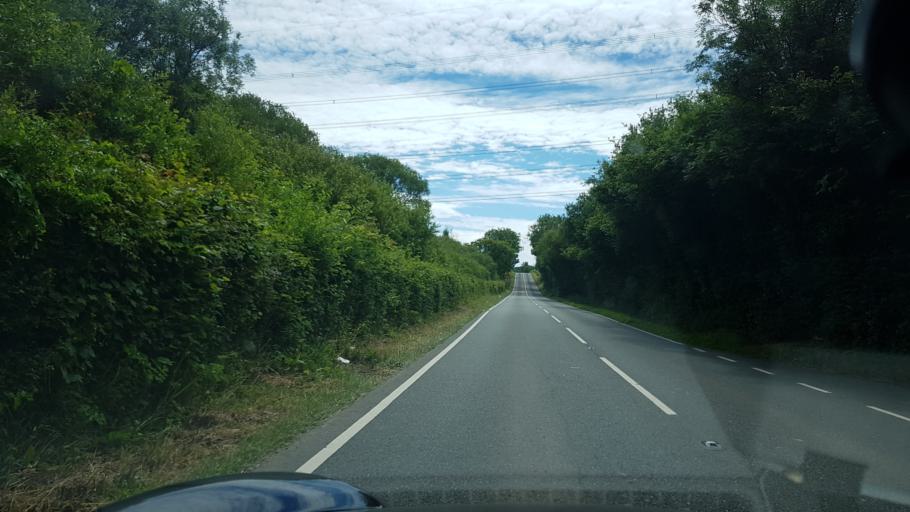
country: GB
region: Wales
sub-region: Carmarthenshire
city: Saint Clears
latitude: 51.7963
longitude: -4.4865
